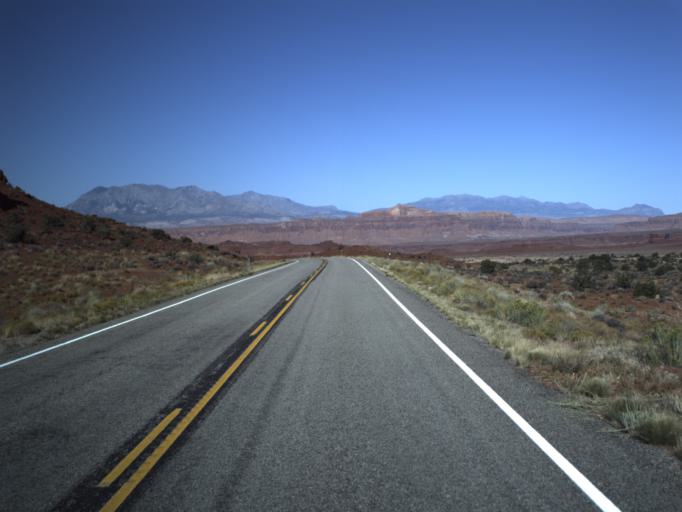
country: US
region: Utah
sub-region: San Juan County
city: Blanding
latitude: 37.8057
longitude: -110.3183
